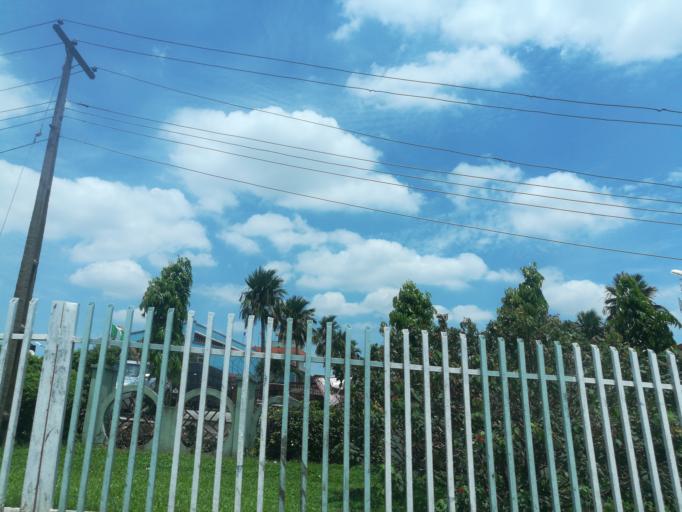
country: NG
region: Lagos
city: Ikeja
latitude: 6.6057
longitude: 3.3475
